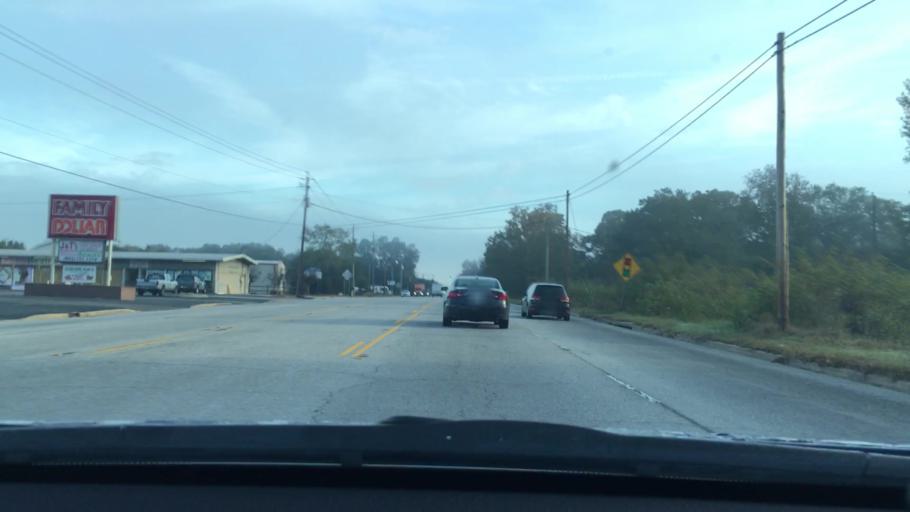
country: US
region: South Carolina
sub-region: Sumter County
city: South Sumter
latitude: 33.8862
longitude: -80.3471
